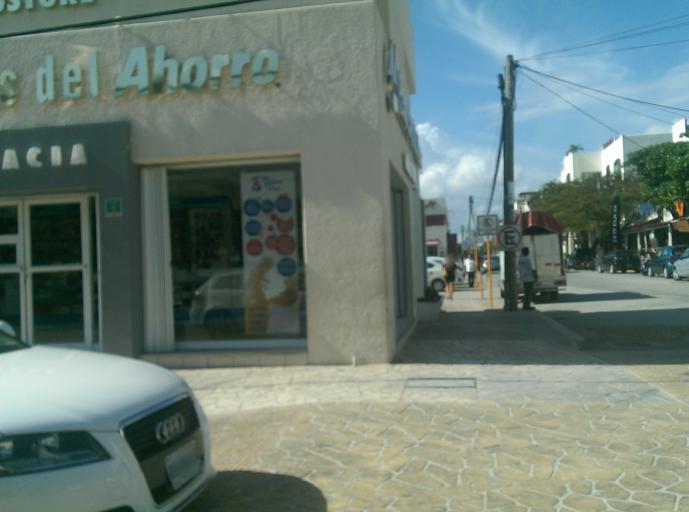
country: MX
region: Quintana Roo
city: Playa del Carmen
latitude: 20.6273
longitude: -87.0732
